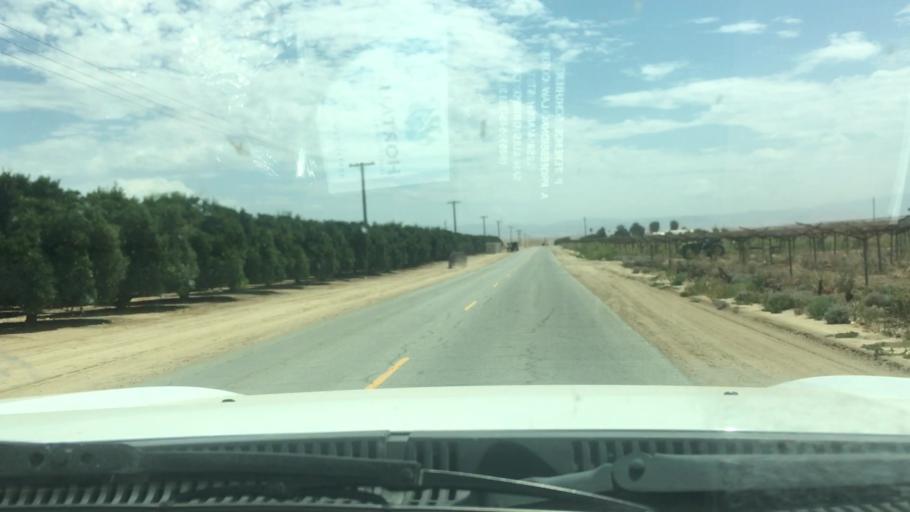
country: US
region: California
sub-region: Kern County
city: McFarland
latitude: 35.6024
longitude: -119.1025
